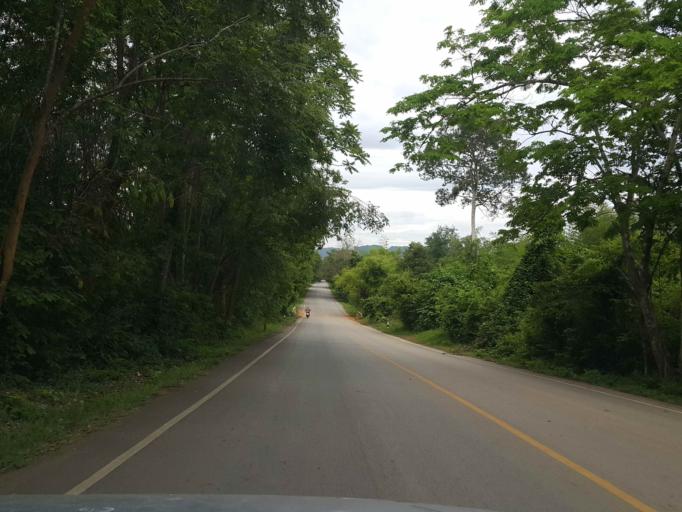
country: TH
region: Sukhothai
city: Thung Saliam
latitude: 17.3506
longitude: 99.4338
